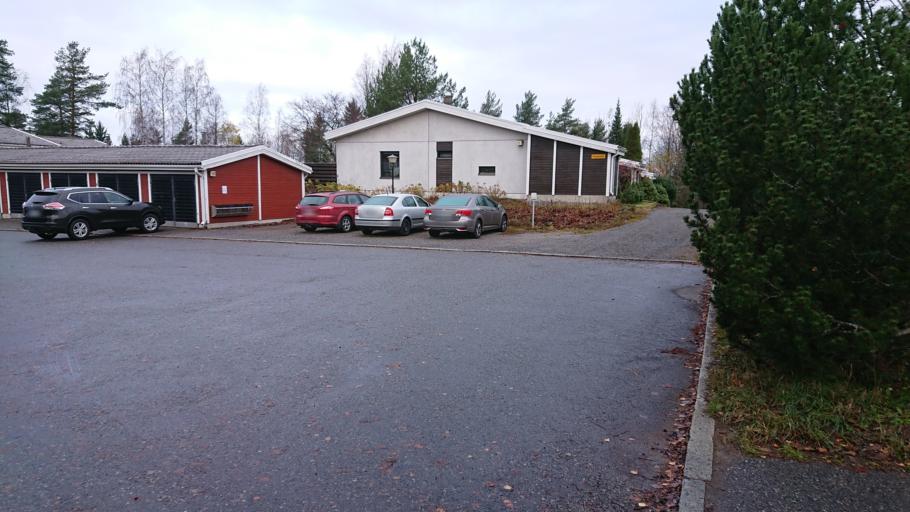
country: FI
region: Pirkanmaa
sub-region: Tampere
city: Tampere
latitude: 61.4548
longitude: 23.8302
